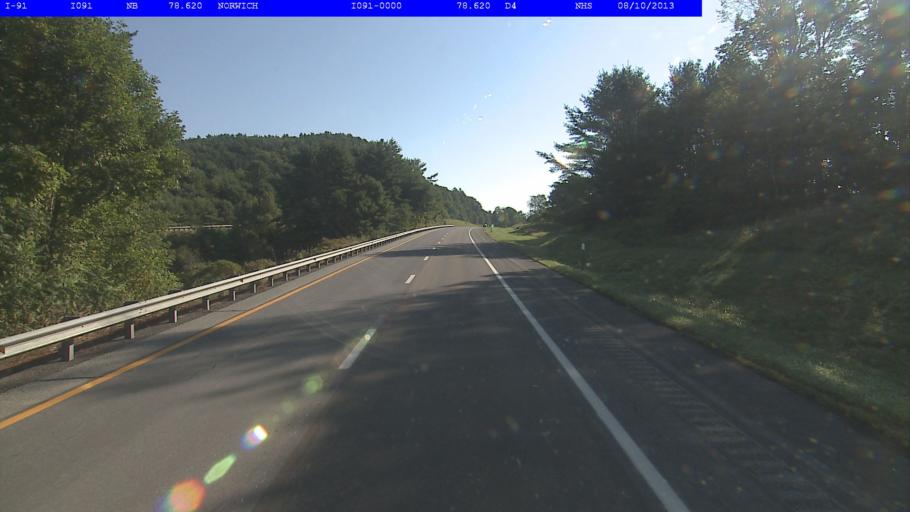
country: US
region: New Hampshire
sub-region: Grafton County
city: Hanover
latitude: 43.7462
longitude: -72.2569
